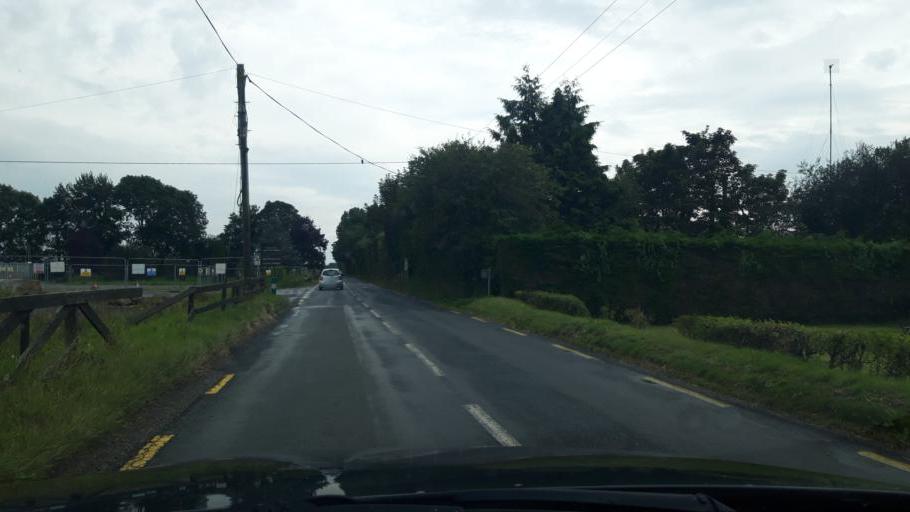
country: IE
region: Leinster
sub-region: Kildare
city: Monasterevin
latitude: 53.0798
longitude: -7.0200
